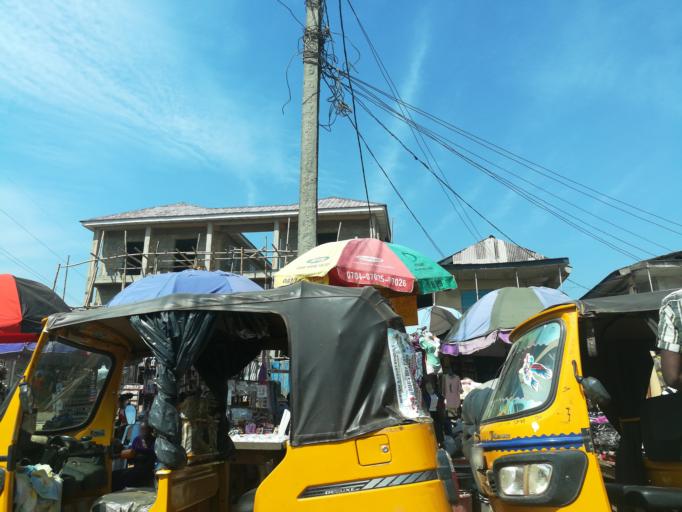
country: NG
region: Lagos
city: Ikorodu
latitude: 6.6266
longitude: 3.4841
